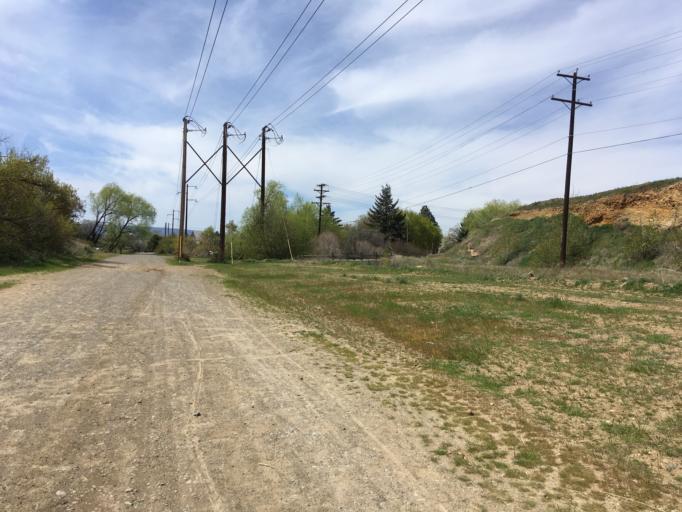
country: US
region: Washington
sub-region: Kittitas County
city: Ellensburg
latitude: 47.0004
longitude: -120.5283
